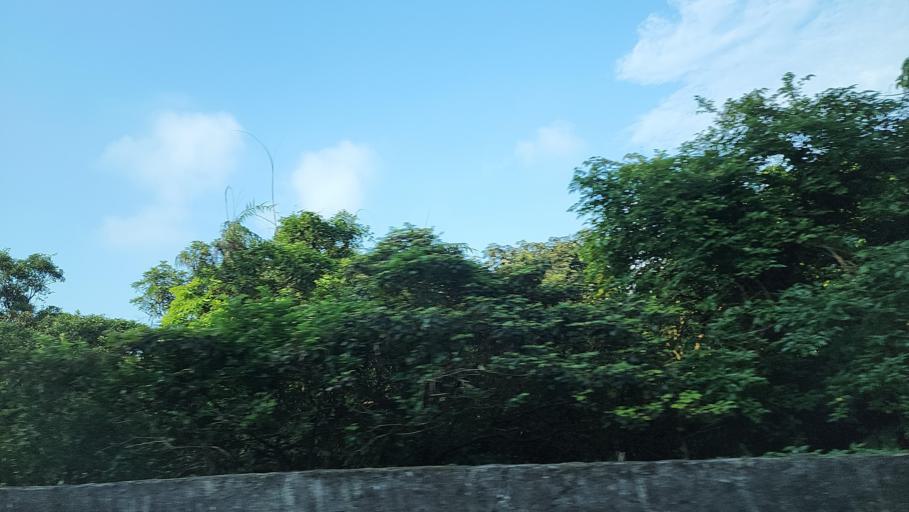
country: TW
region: Taiwan
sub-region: Keelung
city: Keelung
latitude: 25.1768
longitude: 121.6516
